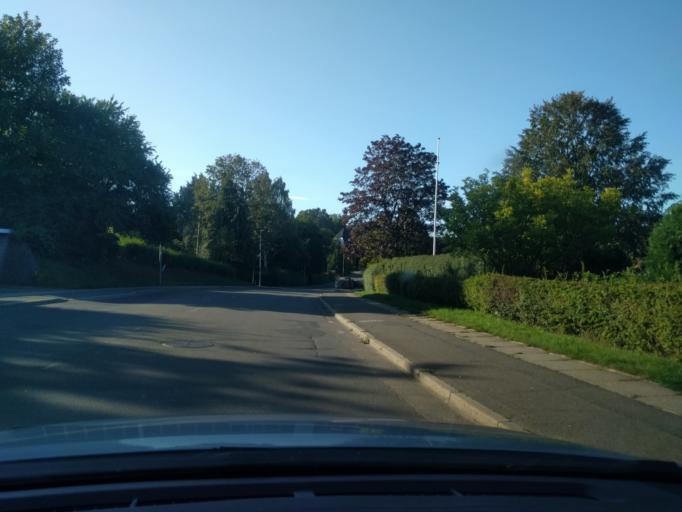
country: DK
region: Central Jutland
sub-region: Horsens Kommune
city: Horsens
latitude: 55.8677
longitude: 9.9001
